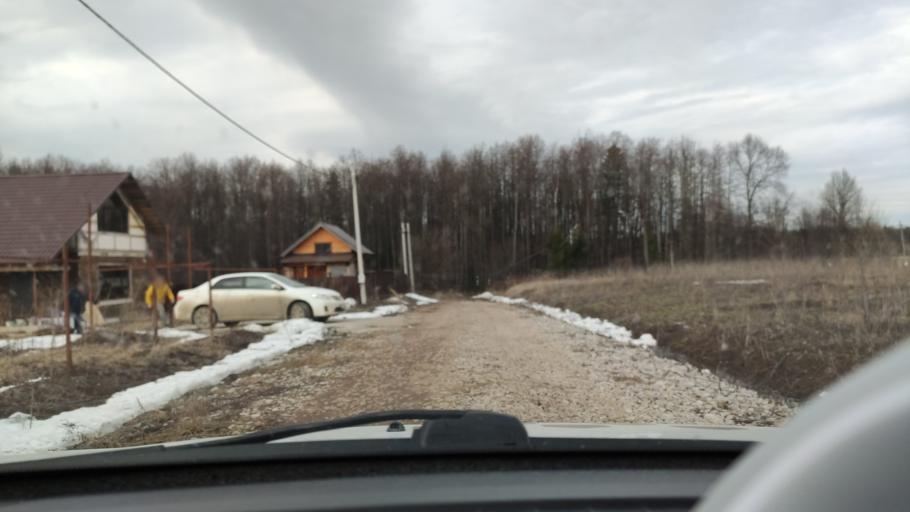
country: RU
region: Perm
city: Ferma
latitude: 57.8835
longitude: 56.3386
